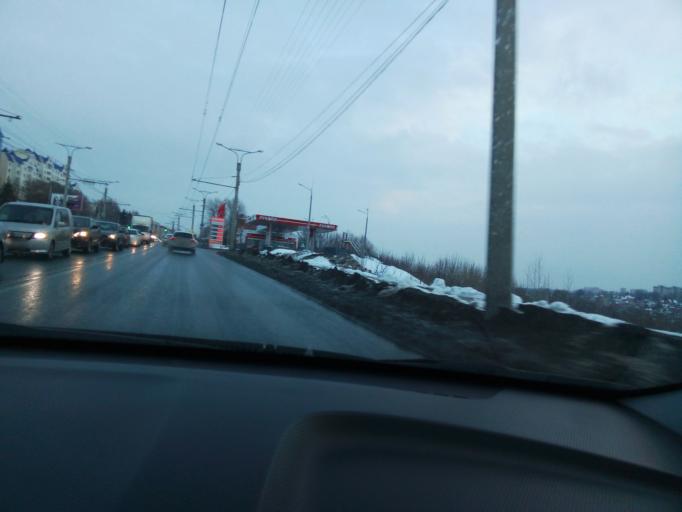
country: RU
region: Chuvashia
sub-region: Cheboksarskiy Rayon
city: Cheboksary
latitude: 56.1316
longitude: 47.2414
